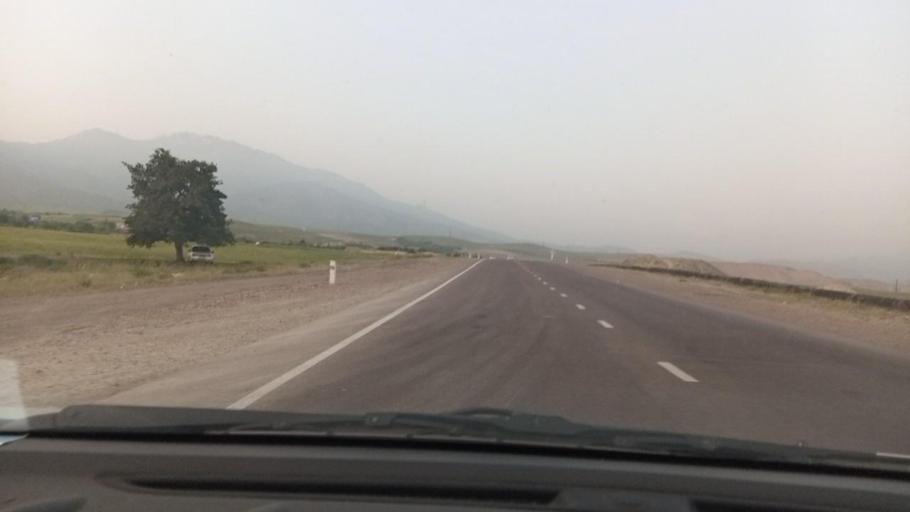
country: UZ
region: Toshkent
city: Angren
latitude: 41.0442
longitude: 70.1561
